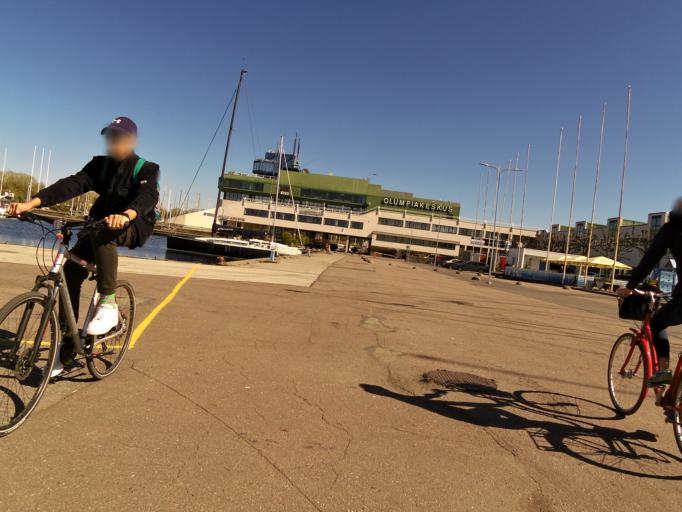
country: EE
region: Harju
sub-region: Viimsi vald
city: Viimsi
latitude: 59.4675
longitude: 24.8249
